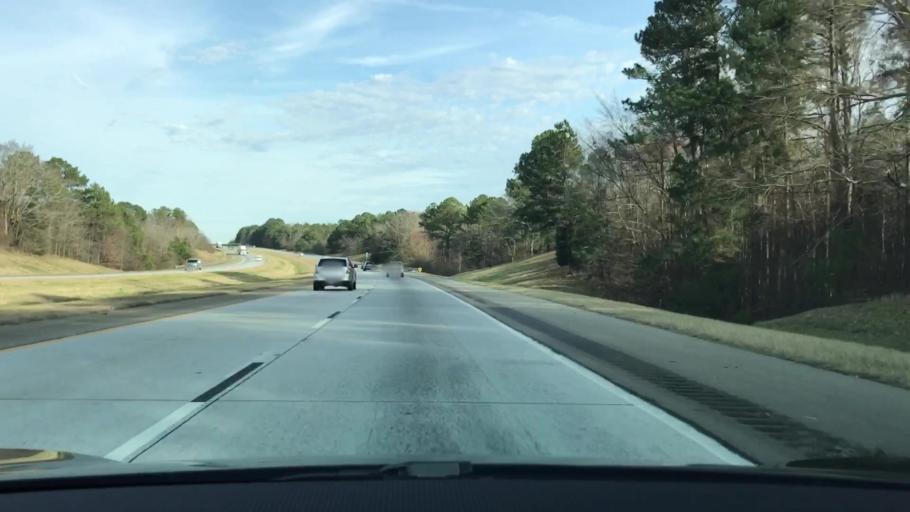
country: US
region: Georgia
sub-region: Greene County
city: Greensboro
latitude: 33.5358
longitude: -83.2467
